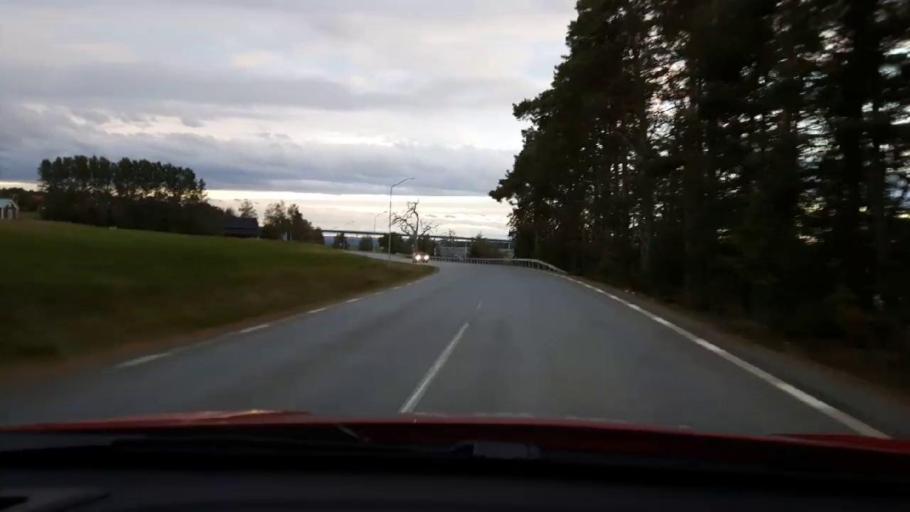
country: SE
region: Jaemtland
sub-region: Bergs Kommun
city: Hoverberg
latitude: 62.9847
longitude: 14.4818
